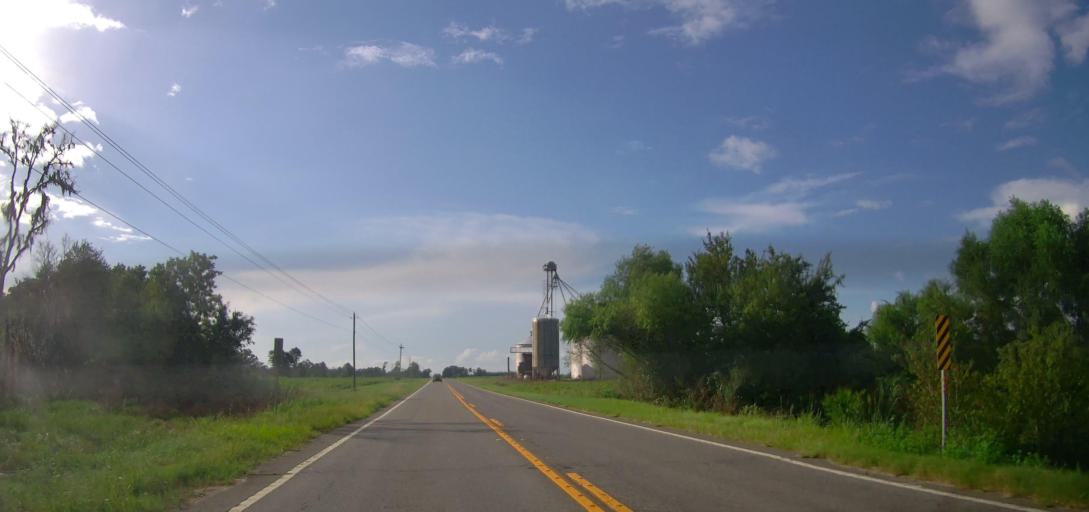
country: US
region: Georgia
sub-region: Coffee County
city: Nicholls
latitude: 31.3452
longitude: -82.6098
